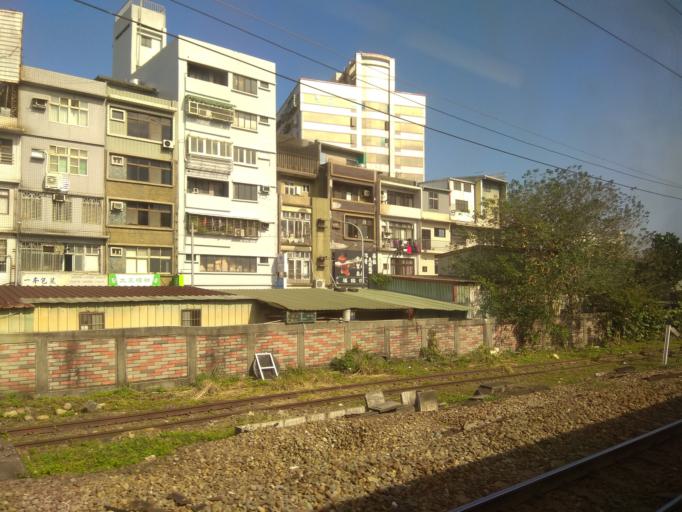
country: TW
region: Taiwan
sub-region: Taoyuan
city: Taoyuan
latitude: 24.9903
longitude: 121.3181
